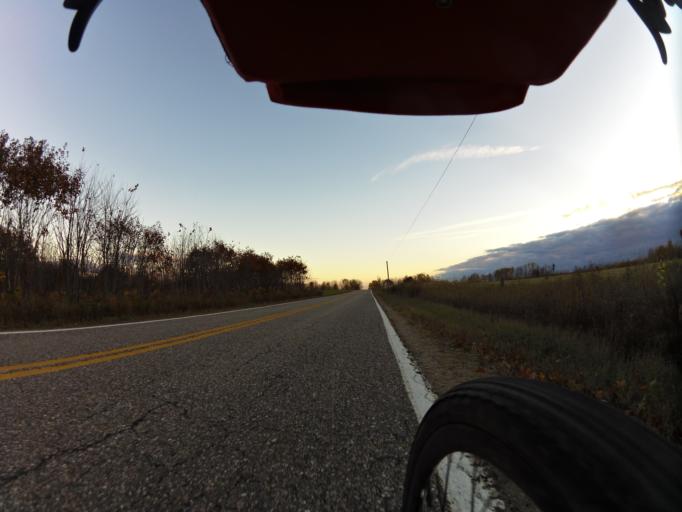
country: CA
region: Ontario
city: Arnprior
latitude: 45.6048
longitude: -76.3044
